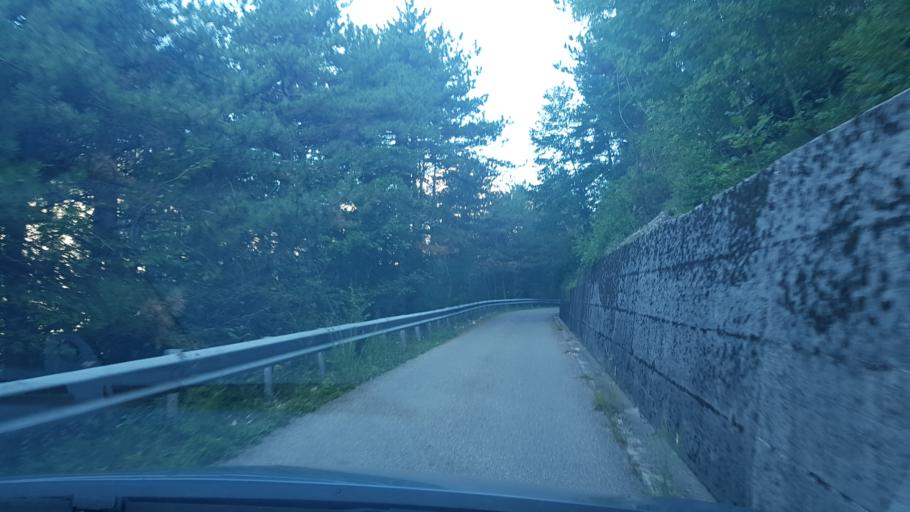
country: IT
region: Friuli Venezia Giulia
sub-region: Provincia di Udine
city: Moggio Udinese
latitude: 46.4339
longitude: 13.2052
